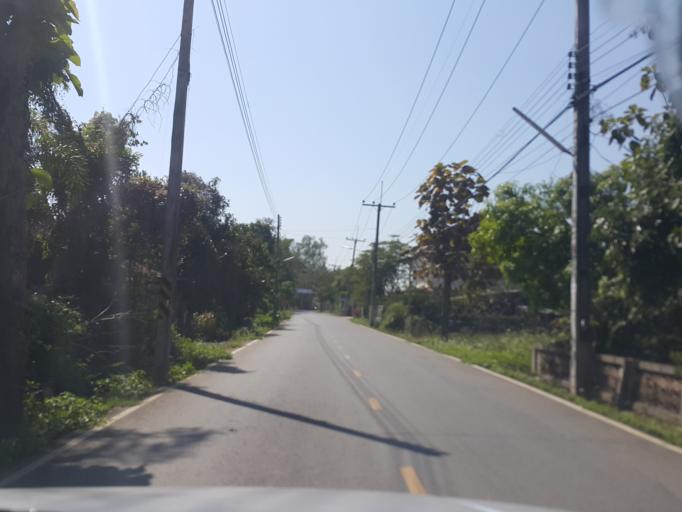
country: TH
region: Chiang Mai
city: San Kamphaeng
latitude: 18.7920
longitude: 99.1301
